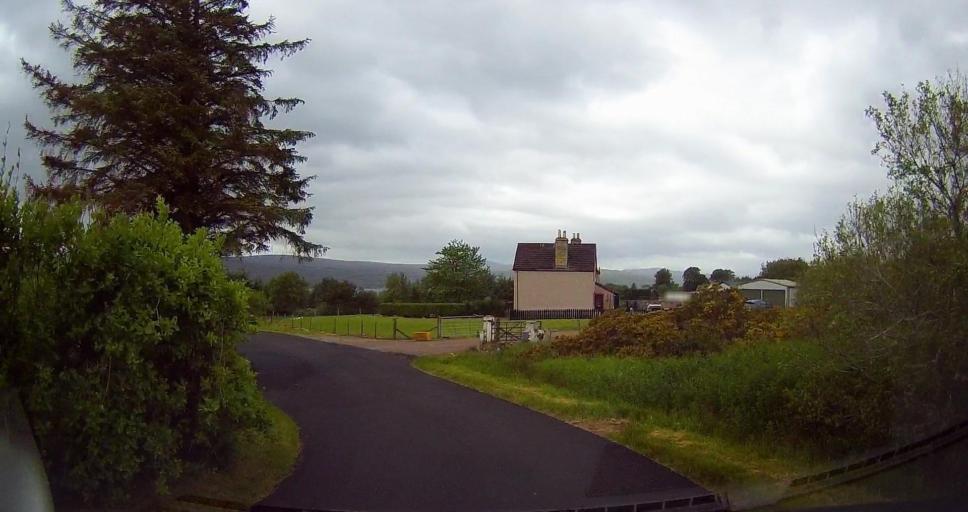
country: GB
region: Scotland
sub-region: Highland
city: Evanton
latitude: 58.0808
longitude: -4.4525
